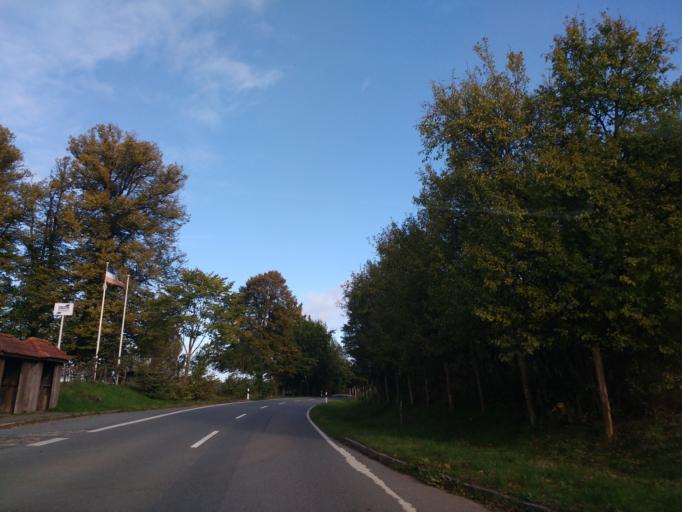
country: DE
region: Schleswig-Holstein
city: Schonwalde am Bungsberg
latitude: 54.2195
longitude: 10.7377
